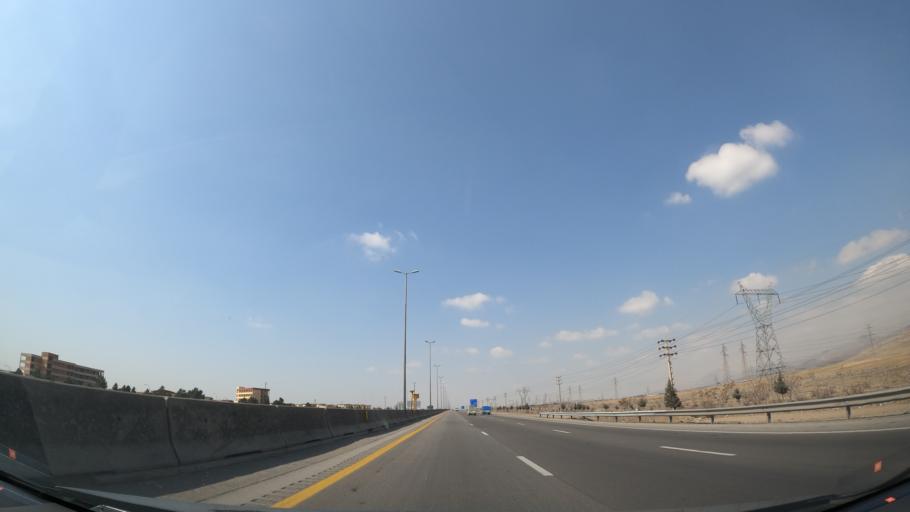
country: IR
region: Qazvin
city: Abyek
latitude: 36.0672
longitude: 50.4852
